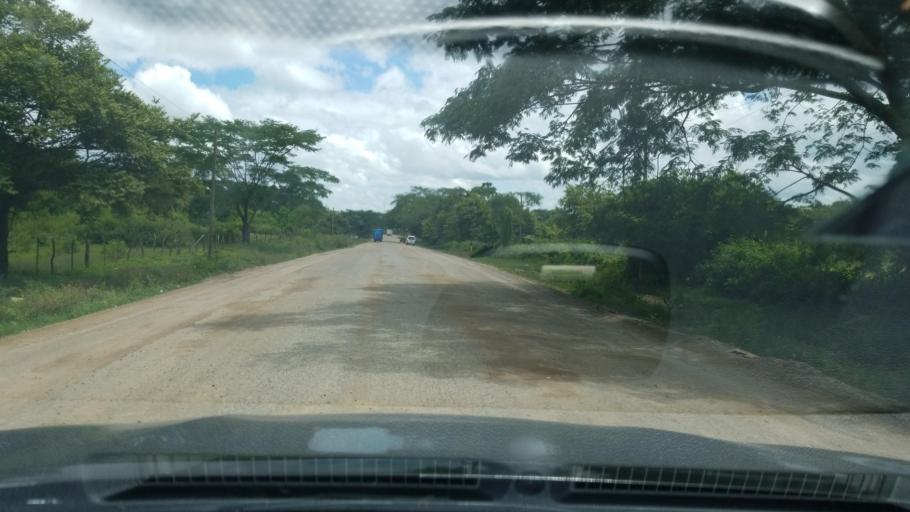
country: HN
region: Francisco Morazan
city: Talanga
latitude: 14.3924
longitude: -87.0767
